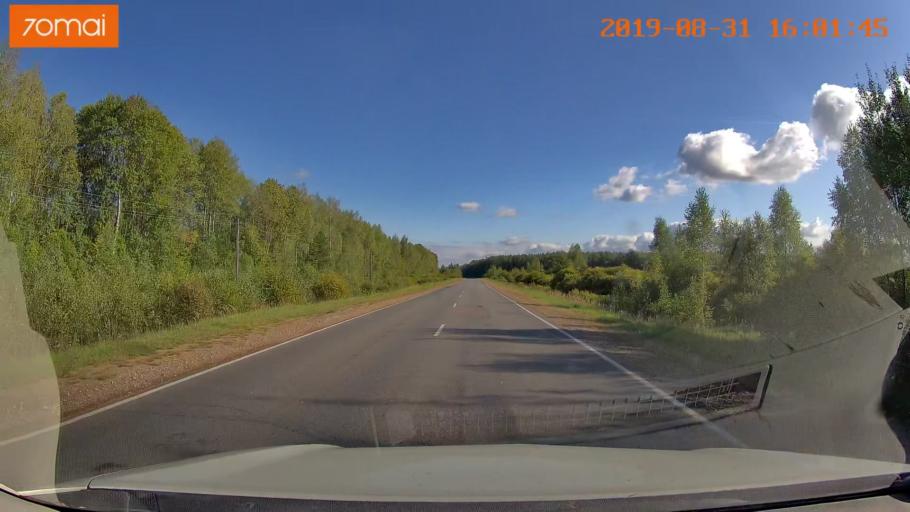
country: RU
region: Kaluga
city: Yukhnov
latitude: 54.6849
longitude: 35.2931
